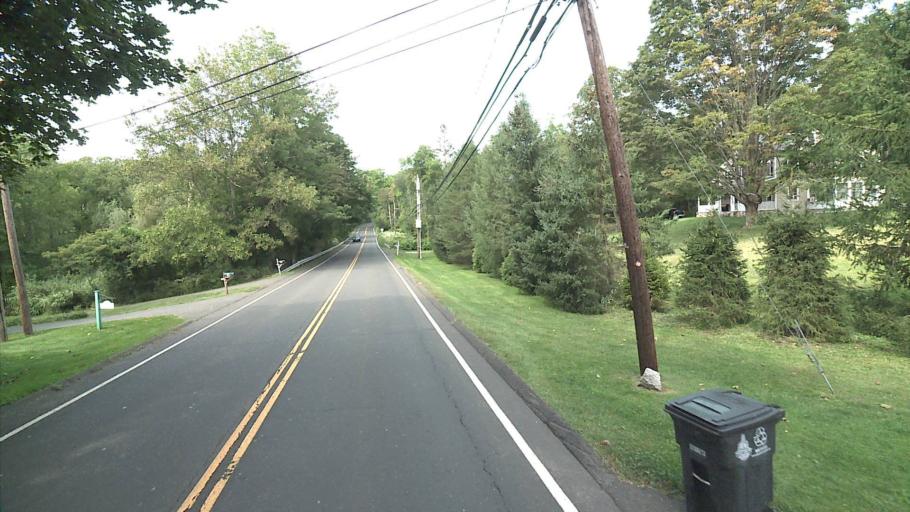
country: US
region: Connecticut
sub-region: Fairfield County
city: North Stamford
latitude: 41.1534
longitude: -73.5942
